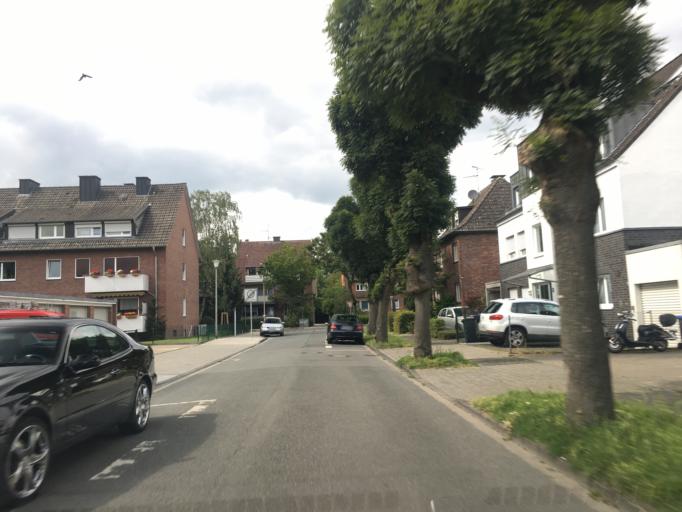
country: DE
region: North Rhine-Westphalia
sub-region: Regierungsbezirk Munster
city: Muenster
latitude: 51.9283
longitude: 7.6701
